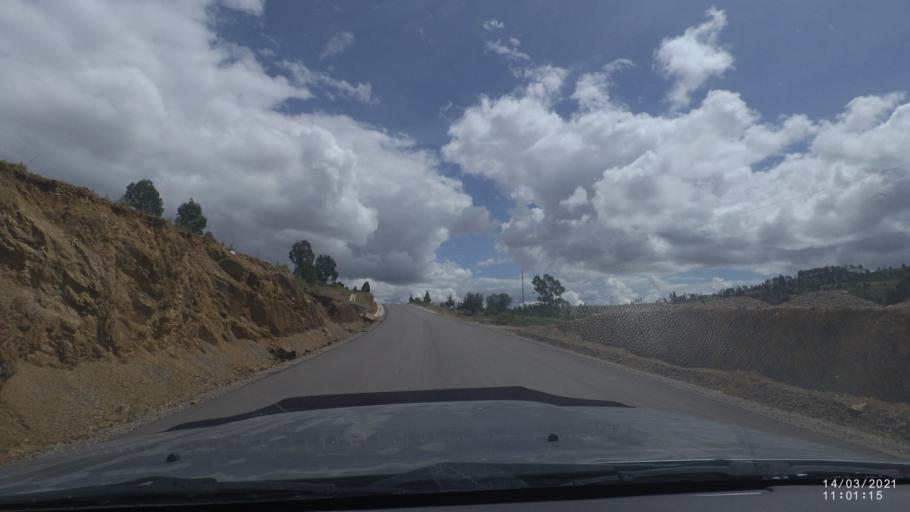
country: BO
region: Cochabamba
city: Tarata
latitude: -17.7968
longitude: -65.9632
